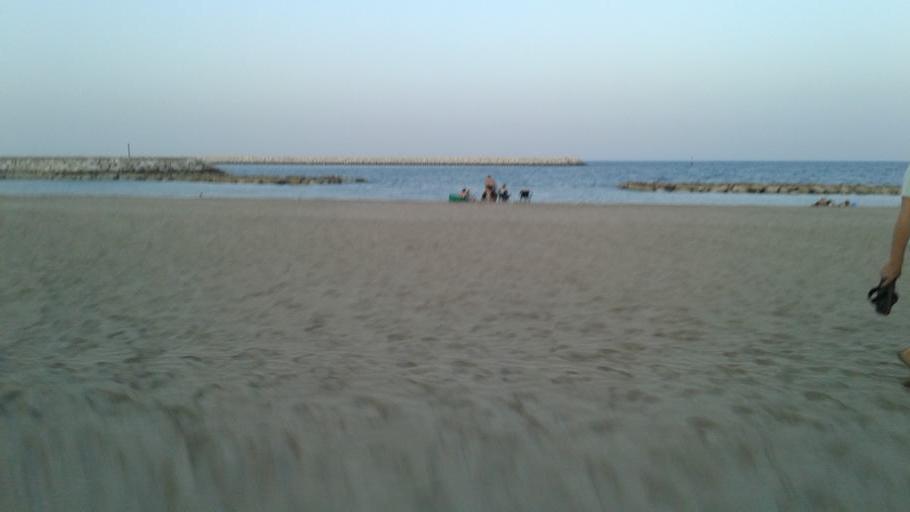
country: OM
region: Muhafazat Masqat
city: As Sib al Jadidah
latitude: 23.6269
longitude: 58.2741
